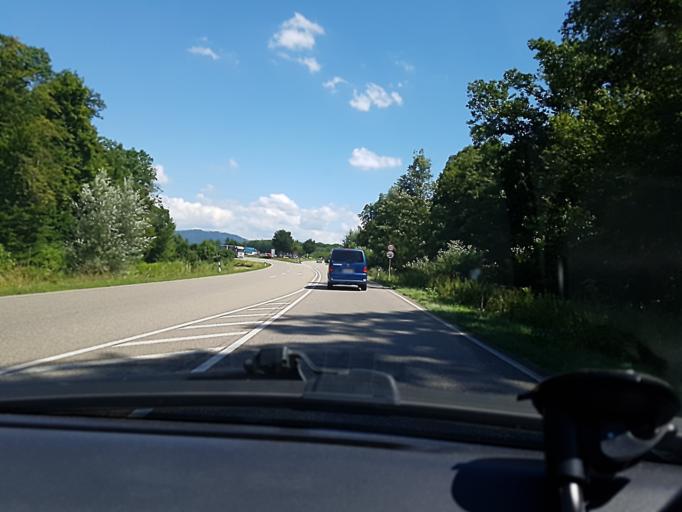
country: DE
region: Baden-Wuerttemberg
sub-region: Freiburg Region
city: Schutterwald
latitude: 48.4734
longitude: 7.8984
